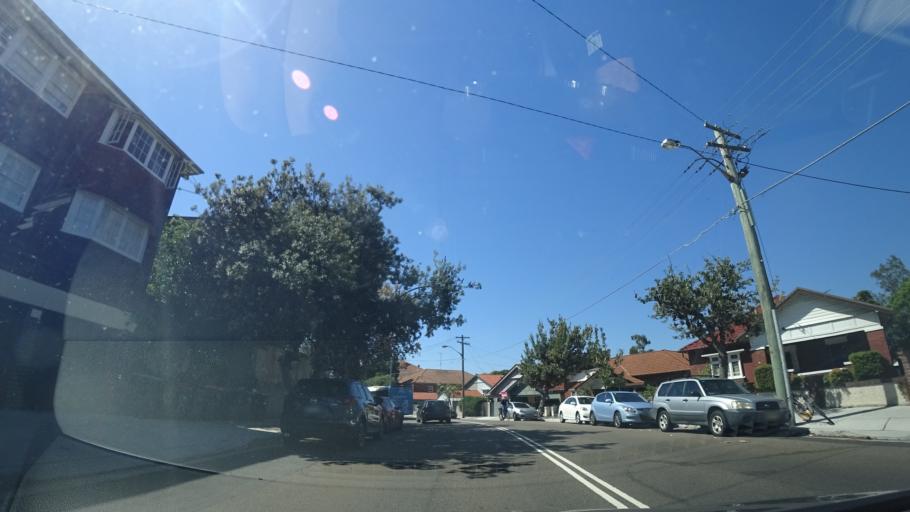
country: AU
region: New South Wales
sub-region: Randwick
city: Randwick
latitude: -33.9107
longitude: 151.2524
